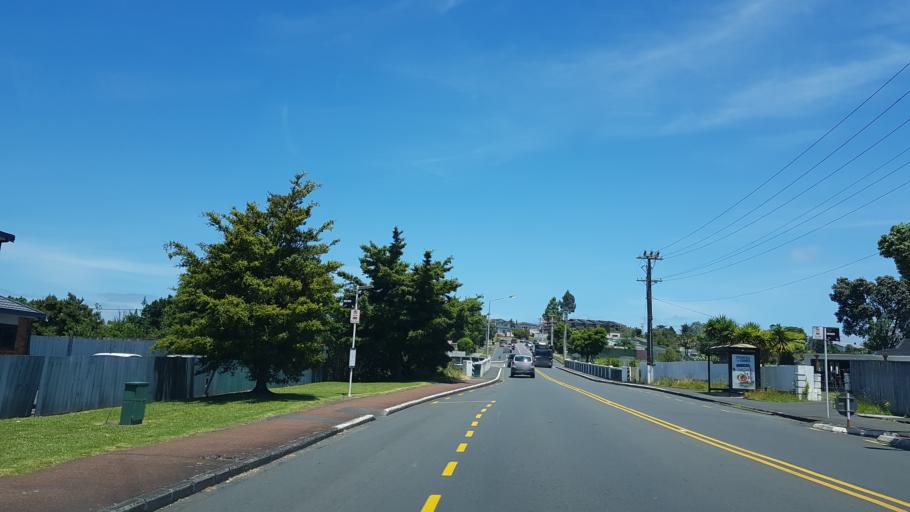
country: NZ
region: Auckland
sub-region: Auckland
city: Waitakere
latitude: -36.9110
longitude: 174.6615
